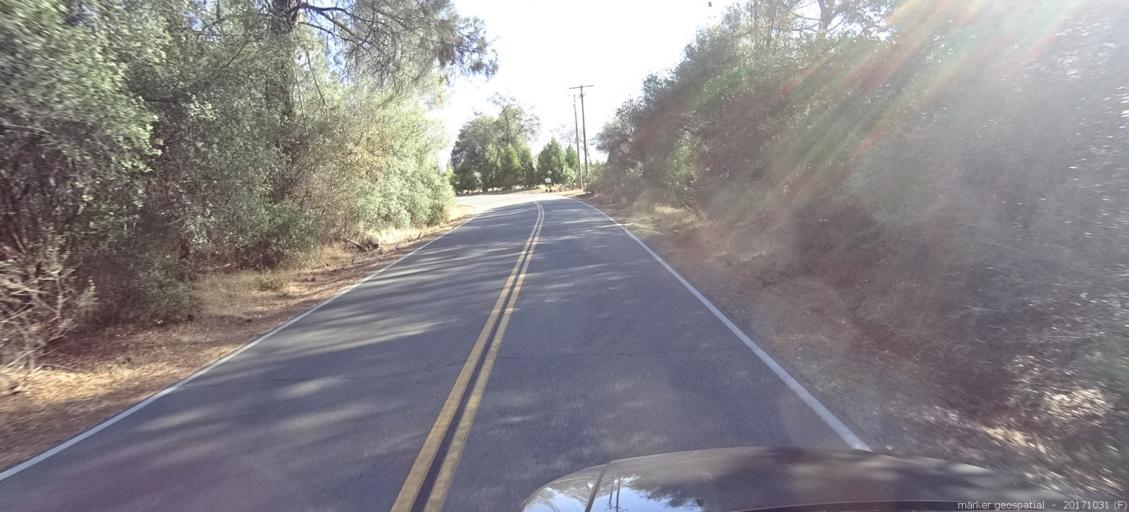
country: US
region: California
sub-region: Shasta County
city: Shingletown
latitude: 40.4463
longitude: -121.8908
